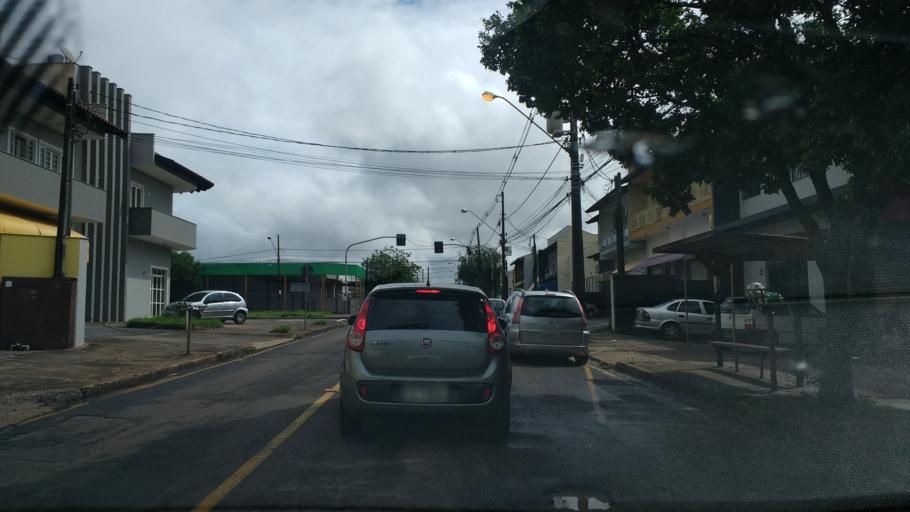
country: BR
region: Parana
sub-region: Londrina
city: Londrina
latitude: -23.3004
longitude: -51.2047
